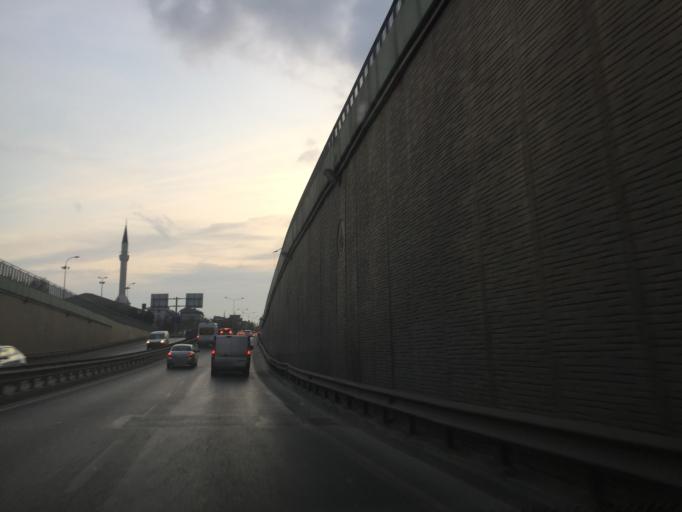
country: TR
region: Istanbul
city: Samandira
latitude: 40.9884
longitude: 29.2255
